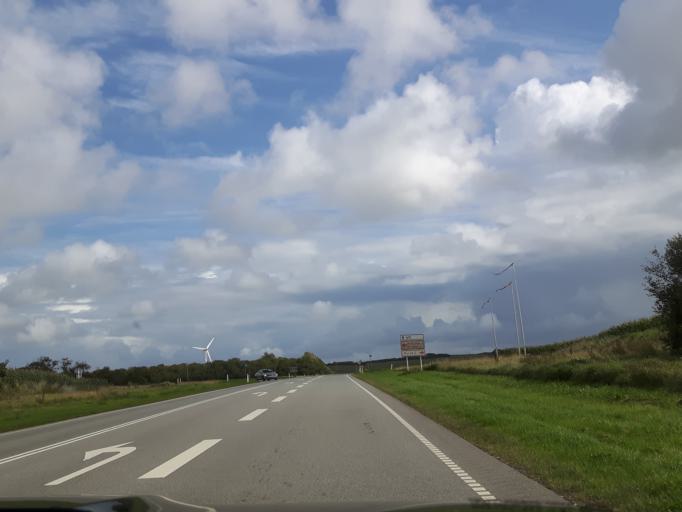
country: DK
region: North Denmark
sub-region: Thisted Kommune
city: Hurup
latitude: 56.7596
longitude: 8.4224
